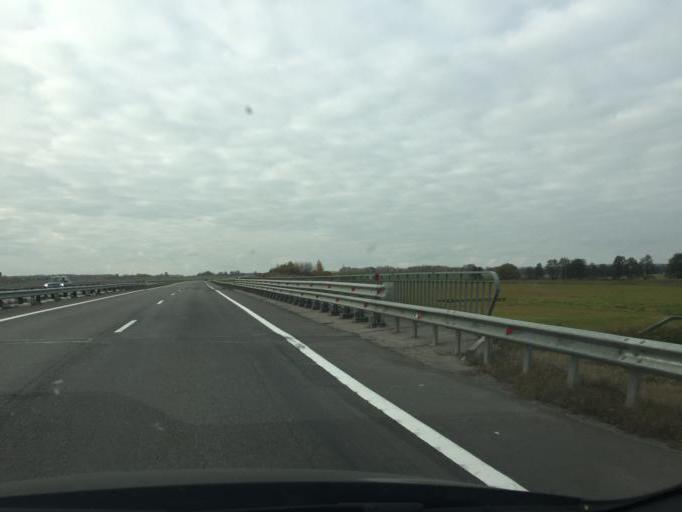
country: BY
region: Minsk
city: Stan'kava
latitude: 53.6757
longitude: 27.2392
